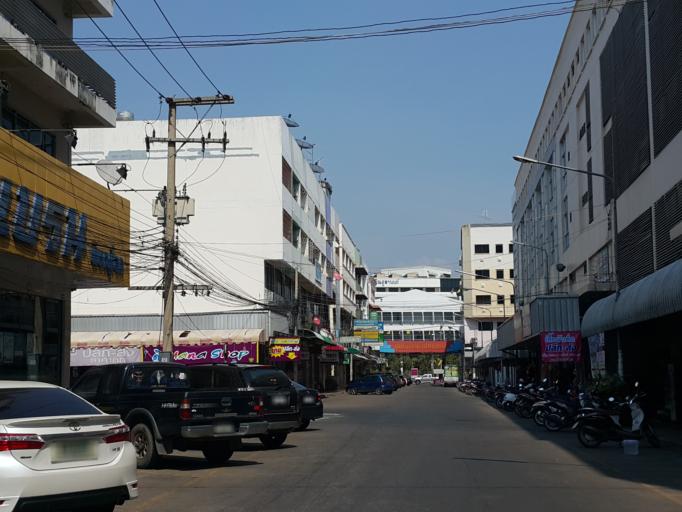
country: TH
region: Phitsanulok
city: Phitsanulok
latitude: 16.8095
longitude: 100.2610
